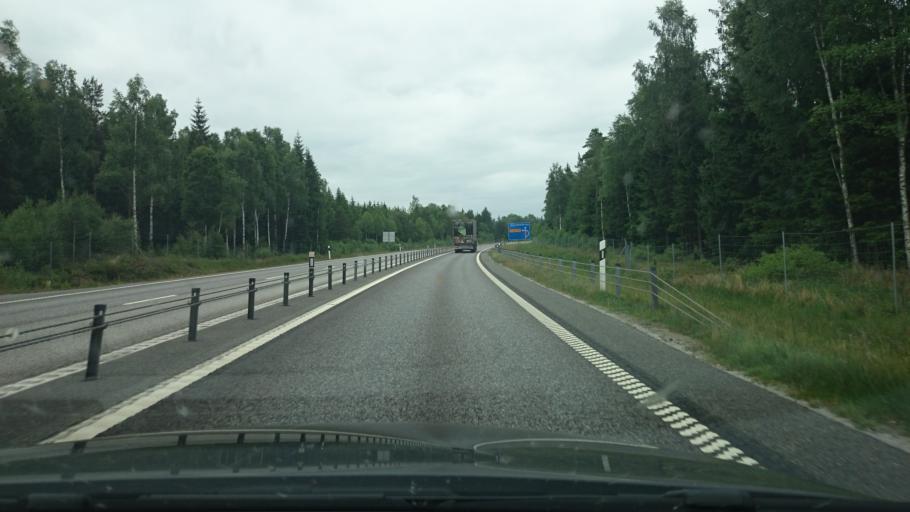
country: SE
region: Halland
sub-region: Hylte Kommun
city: Hyltebruk
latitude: 56.9749
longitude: 13.1767
